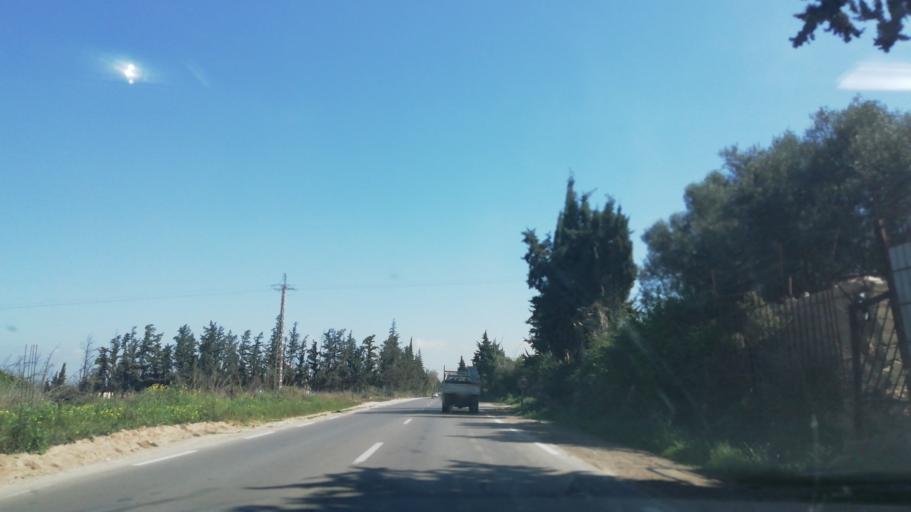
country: DZ
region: Mascara
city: Sig
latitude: 35.5773
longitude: 0.0037
